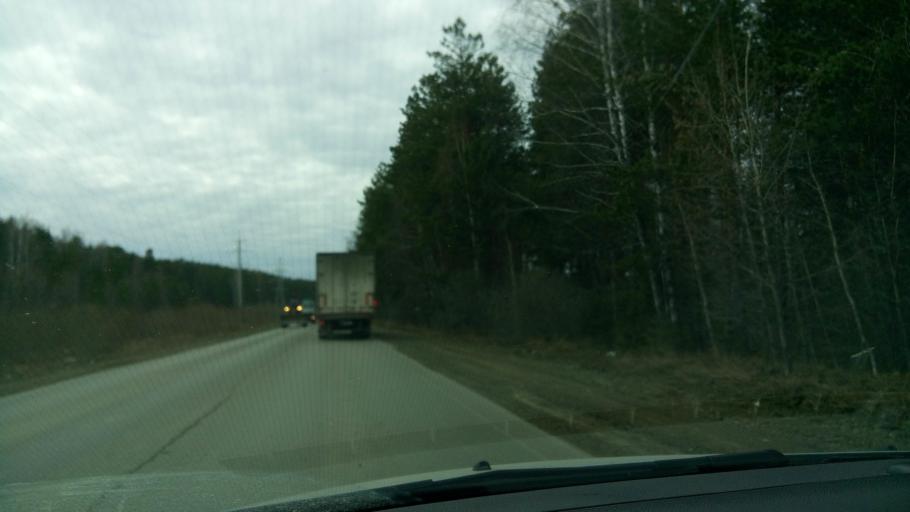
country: RU
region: Sverdlovsk
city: Verkhnyaya Pyshma
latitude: 56.9525
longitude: 60.6432
